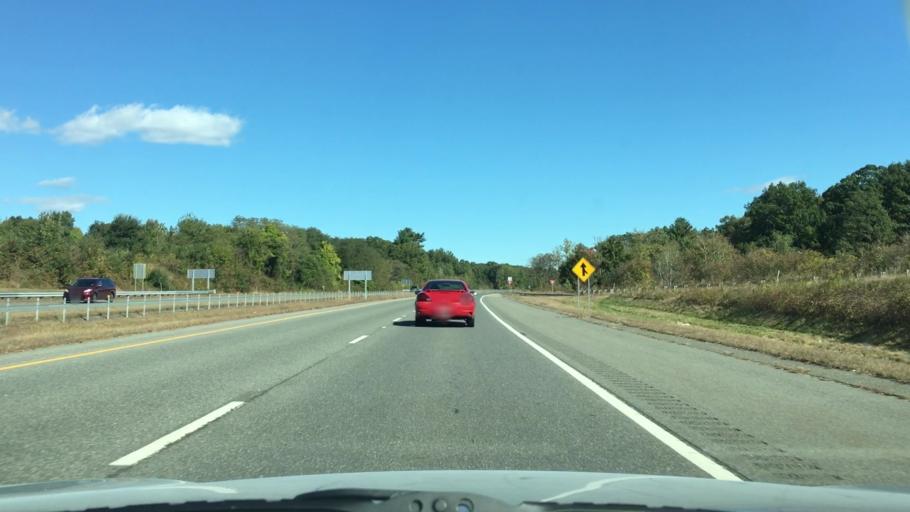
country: US
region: Massachusetts
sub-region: Hampden County
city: Agawam
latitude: 42.0642
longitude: -72.6557
